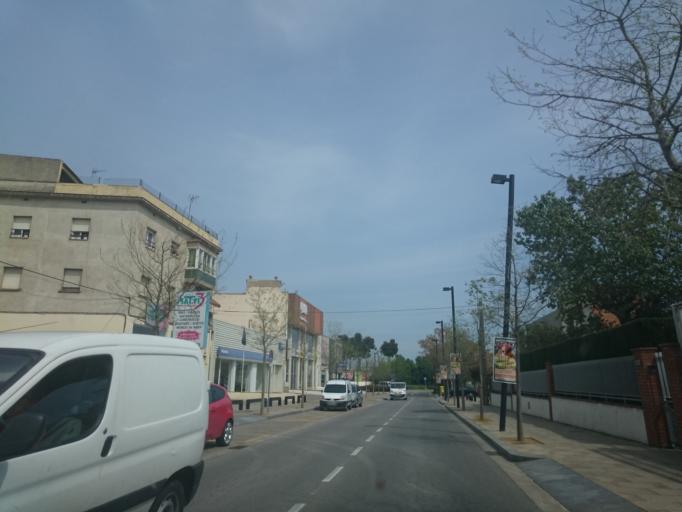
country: ES
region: Catalonia
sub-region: Provincia de Girona
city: Figueres
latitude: 42.2666
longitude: 2.9756
